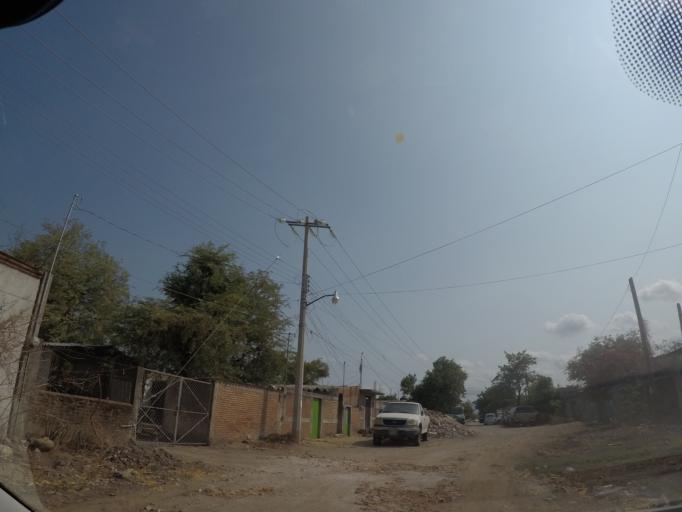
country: MX
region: Oaxaca
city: San Jeronimo Ixtepec
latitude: 16.5503
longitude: -95.0842
